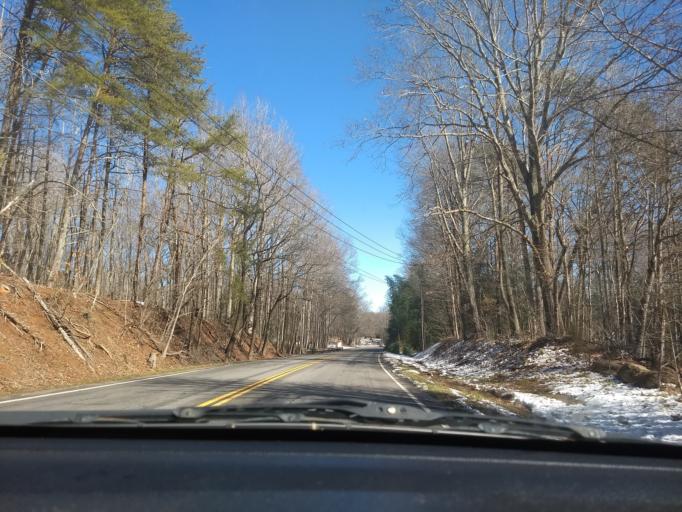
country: US
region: South Carolina
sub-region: Greenville County
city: Sans Souci
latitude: 34.9067
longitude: -82.3833
